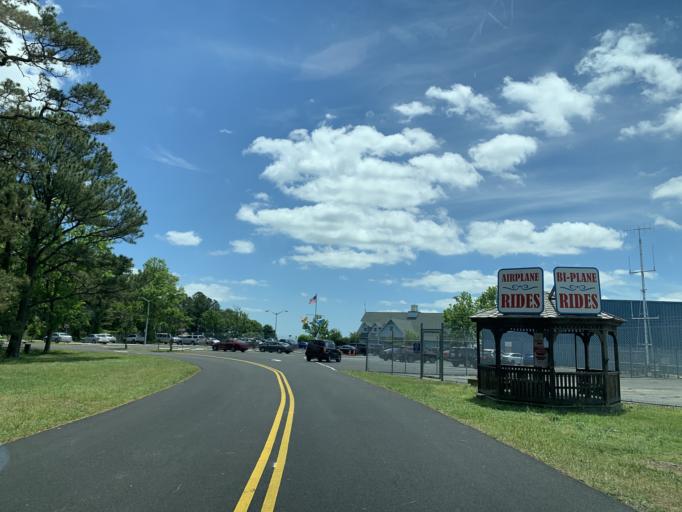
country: US
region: Maryland
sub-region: Worcester County
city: West Ocean City
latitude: 38.3116
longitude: -75.1186
